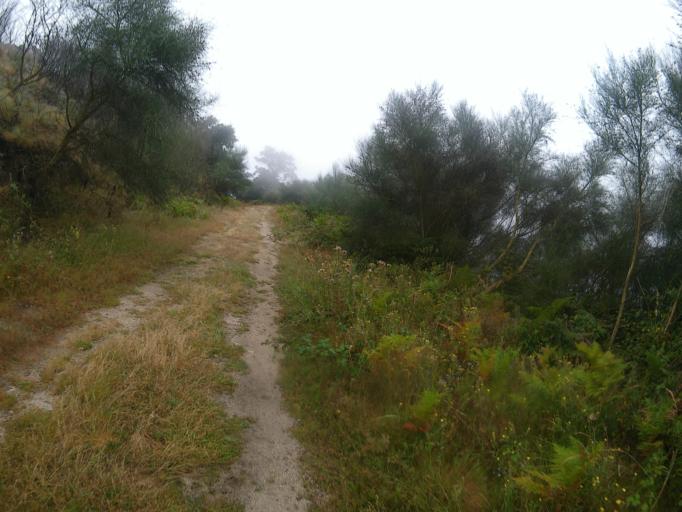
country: PT
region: Viana do Castelo
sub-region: Ponte de Lima
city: Ponte de Lima
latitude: 41.7111
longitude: -8.6058
